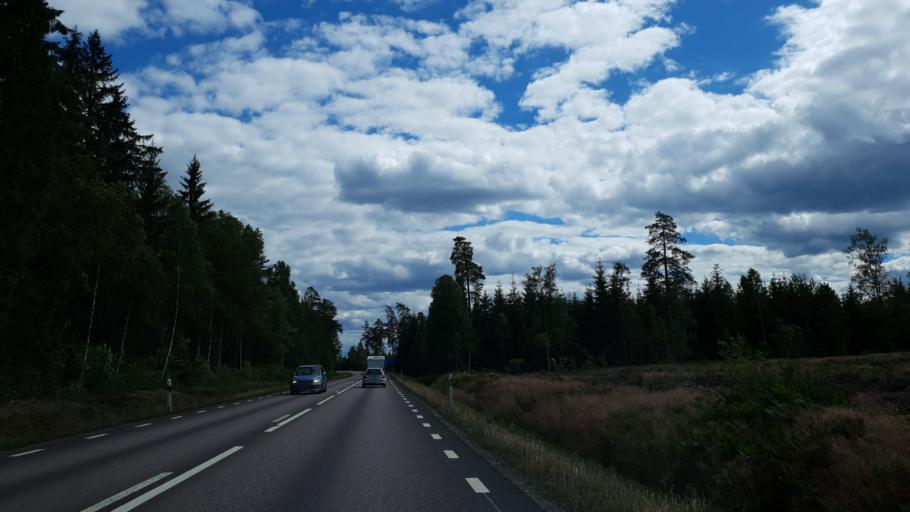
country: SE
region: Kronoberg
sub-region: Lessebo Kommun
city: Lessebo
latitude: 56.8369
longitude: 15.3923
